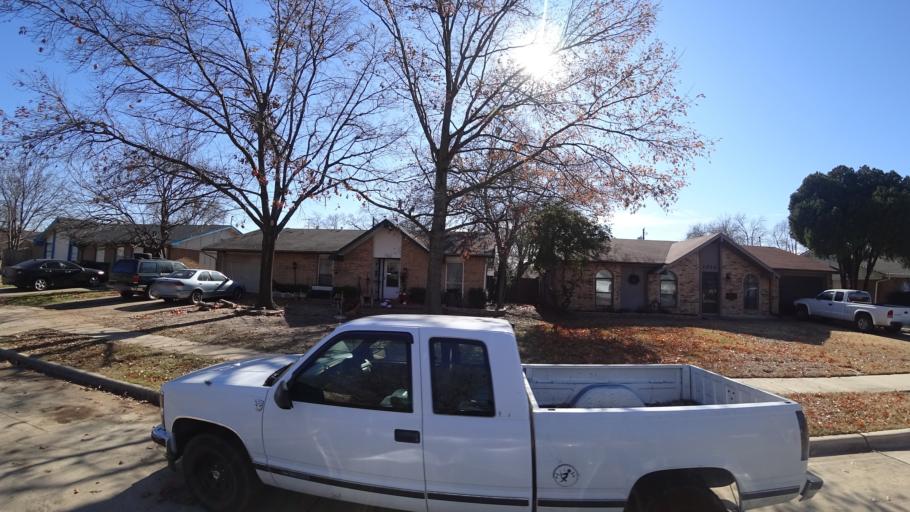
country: US
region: Texas
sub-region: Denton County
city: Lewisville
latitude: 33.0339
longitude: -97.0221
